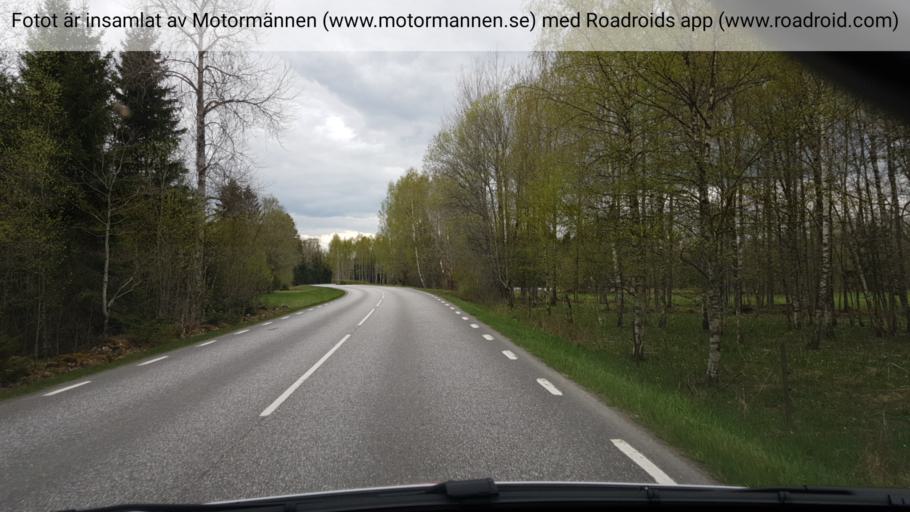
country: SE
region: Vaestra Goetaland
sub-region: Falkopings Kommun
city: Floby
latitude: 58.0459
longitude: 13.1973
